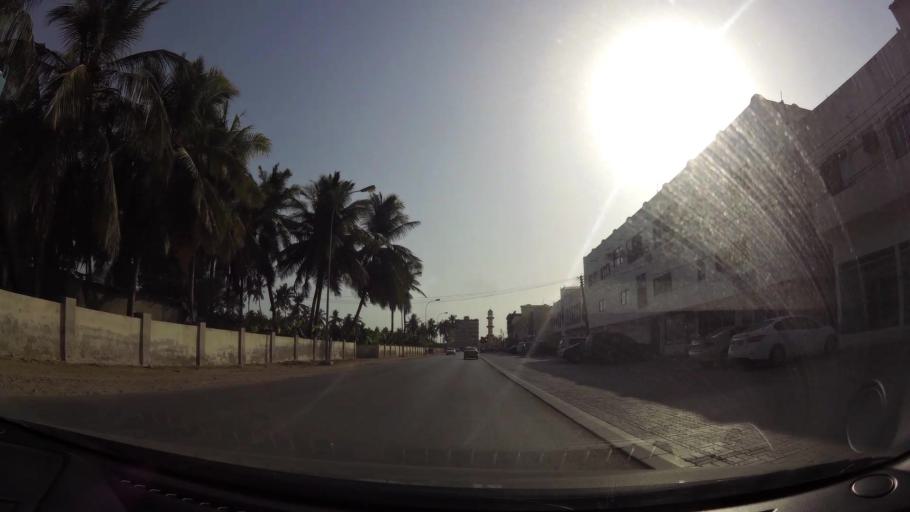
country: OM
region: Zufar
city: Salalah
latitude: 17.0079
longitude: 54.0828
